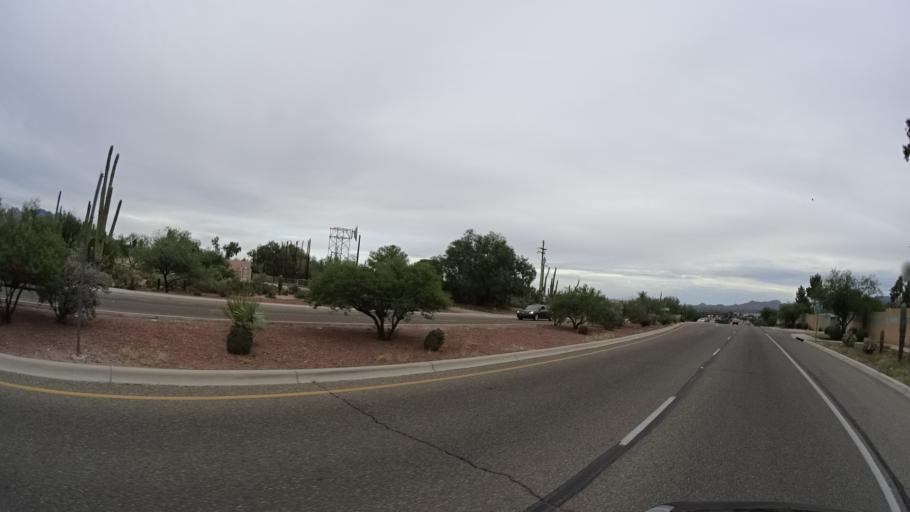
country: US
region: Arizona
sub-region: Pima County
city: Casas Adobes
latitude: 32.3435
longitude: -111.0470
